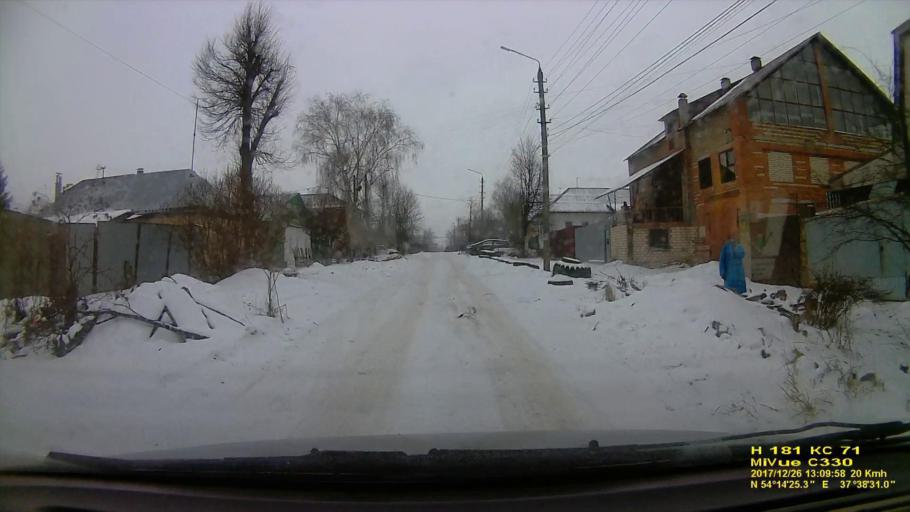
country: RU
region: Tula
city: Gorelki
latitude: 54.2404
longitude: 37.6420
